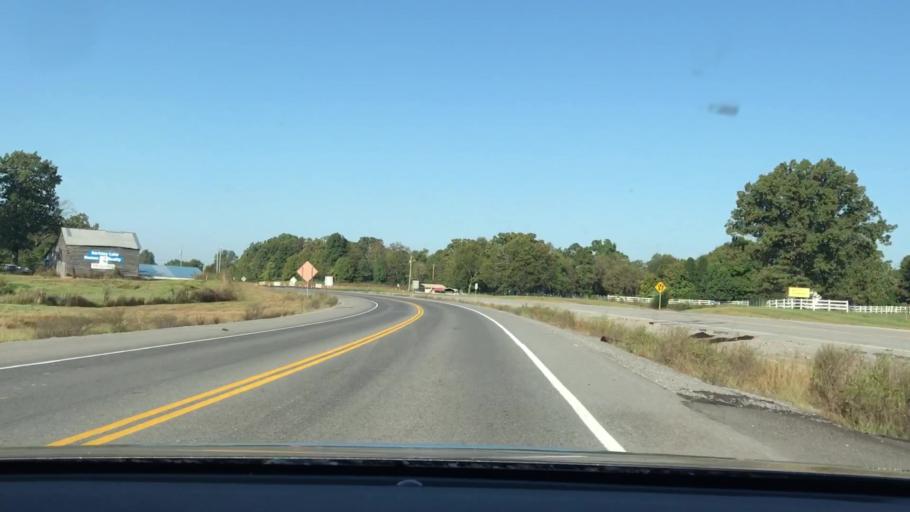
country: US
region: Kentucky
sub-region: Trigg County
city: Cadiz
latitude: 36.8392
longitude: -87.8563
